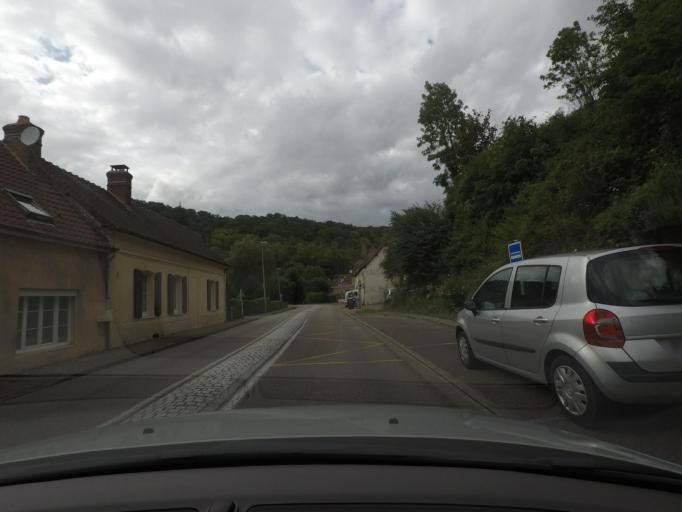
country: FR
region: Haute-Normandie
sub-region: Departement de l'Eure
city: Les Andelys
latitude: 49.2532
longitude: 1.3802
